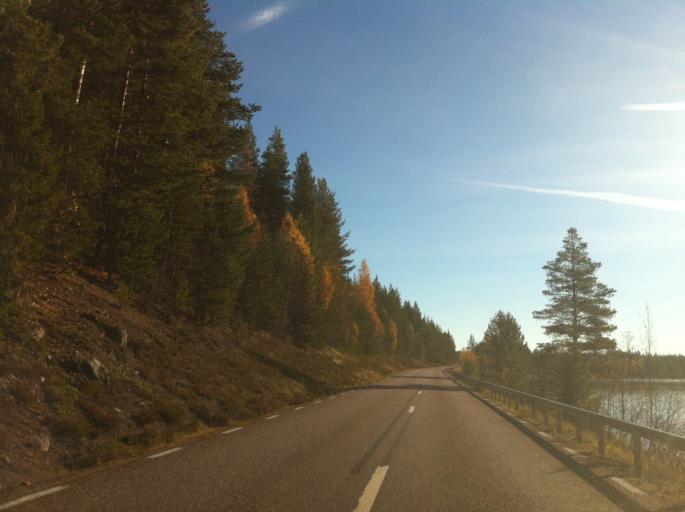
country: NO
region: Hedmark
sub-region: Trysil
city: Innbygda
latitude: 61.8244
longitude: 12.8831
